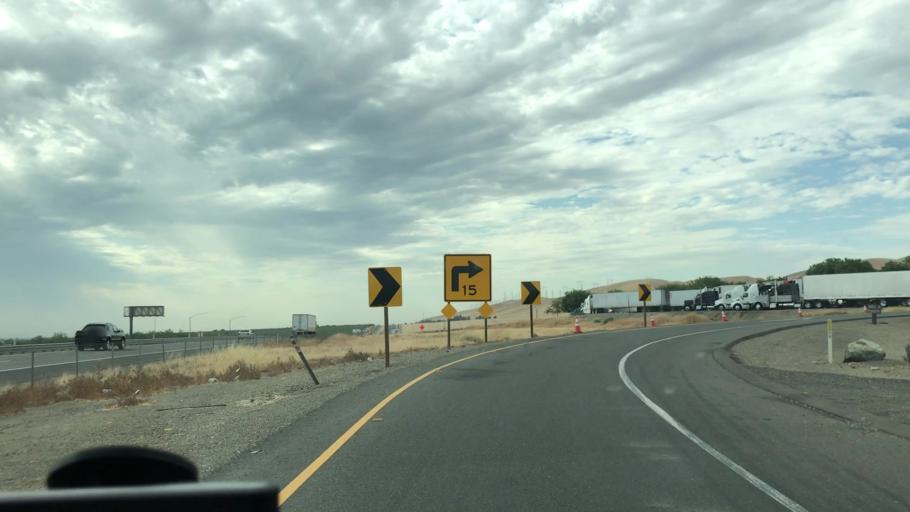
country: US
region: California
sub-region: San Joaquin County
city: Tracy
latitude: 37.5830
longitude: -121.3239
